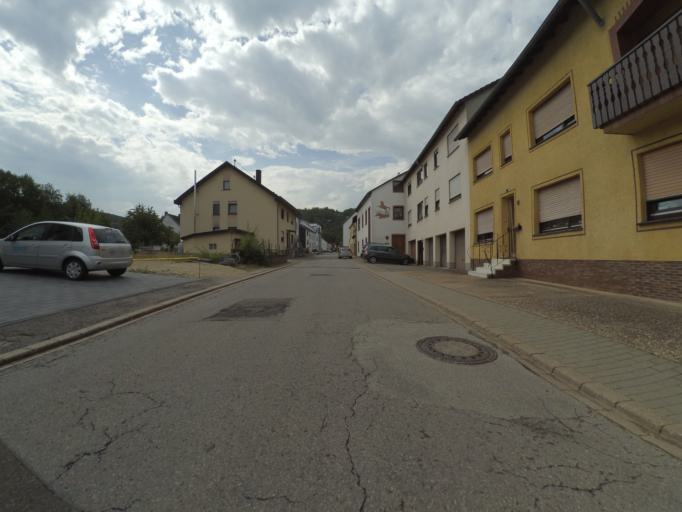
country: DE
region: Rheinland-Pfalz
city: Tawern
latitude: 49.6713
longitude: 6.5143
